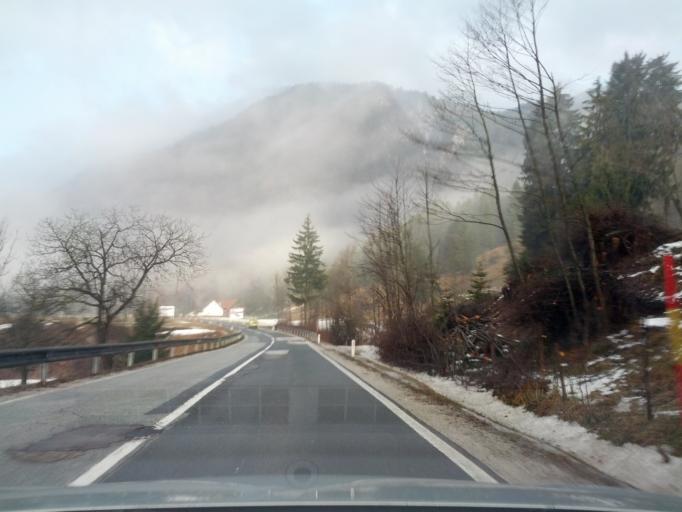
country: SI
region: Kranjska Gora
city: Mojstrana
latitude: 46.4731
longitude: 13.9140
